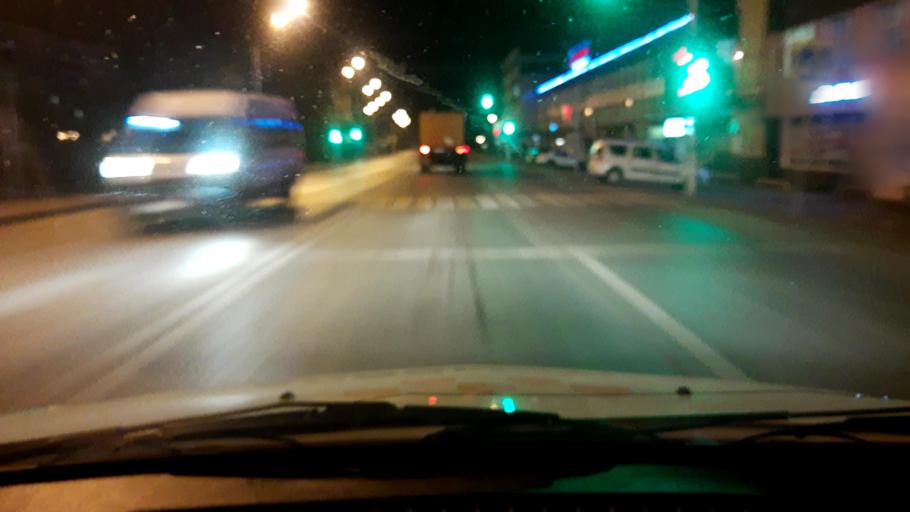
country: RU
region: Bashkortostan
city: Iglino
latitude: 54.7579
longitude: 56.2468
